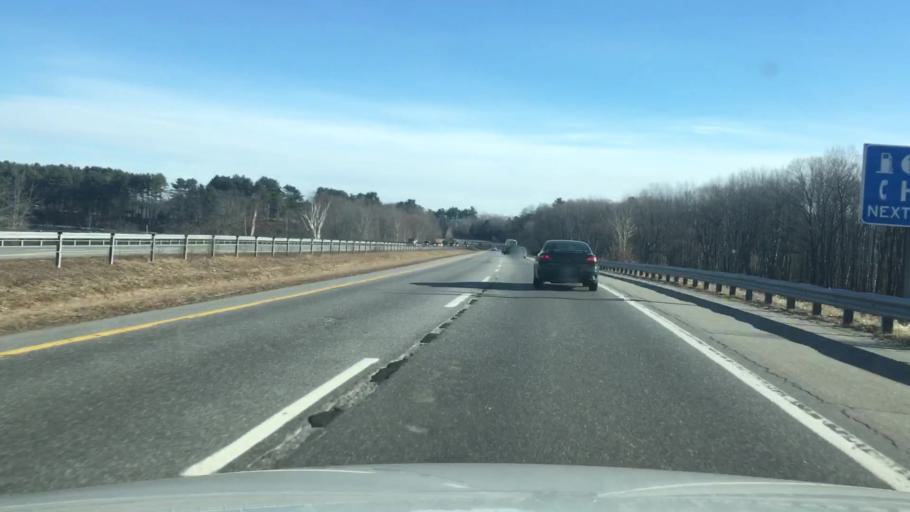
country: US
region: Maine
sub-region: Cumberland County
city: Brunswick
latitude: 43.9109
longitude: -69.9355
